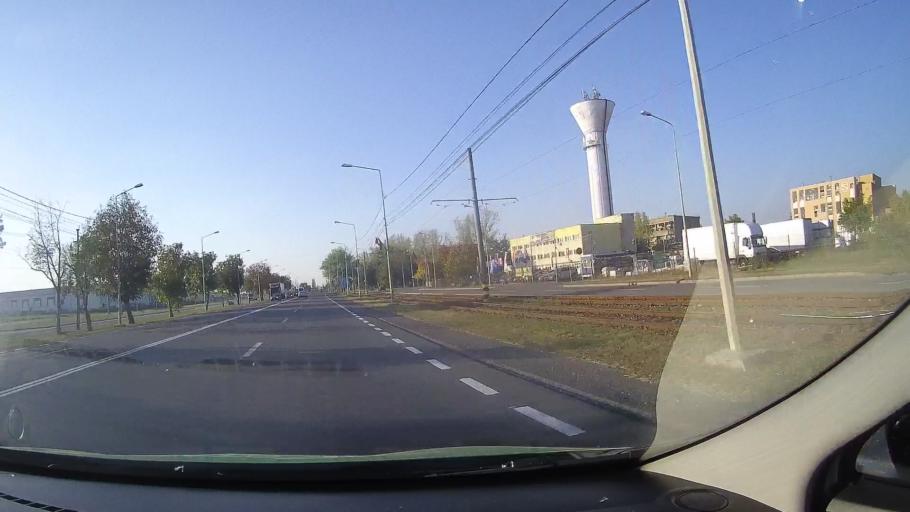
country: RO
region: Bihor
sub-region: Comuna Santandrei
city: Santandrei
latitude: 47.0861
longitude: 21.8814
